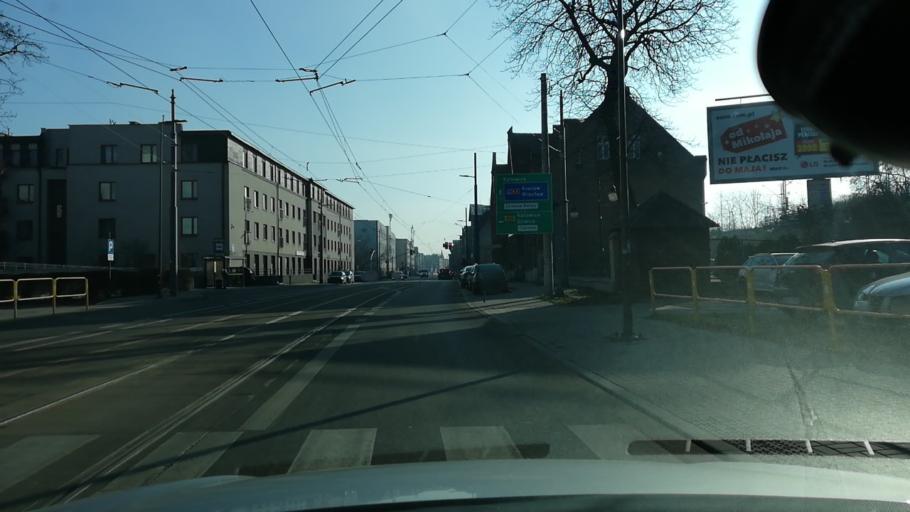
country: PL
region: Silesian Voivodeship
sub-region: Swietochlowice
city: Swietochlowice
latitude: 50.2829
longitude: 18.9369
